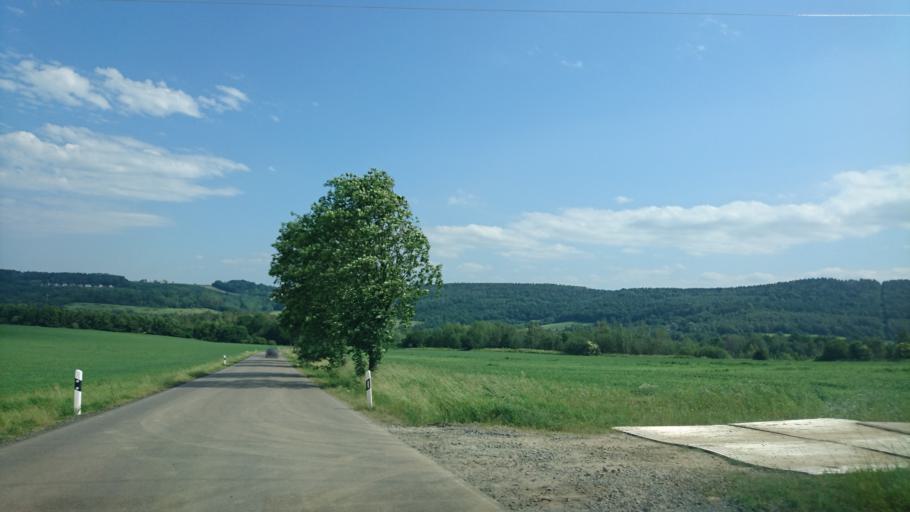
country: DE
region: Saxony
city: Dohma
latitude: 50.9073
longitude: 13.9698
